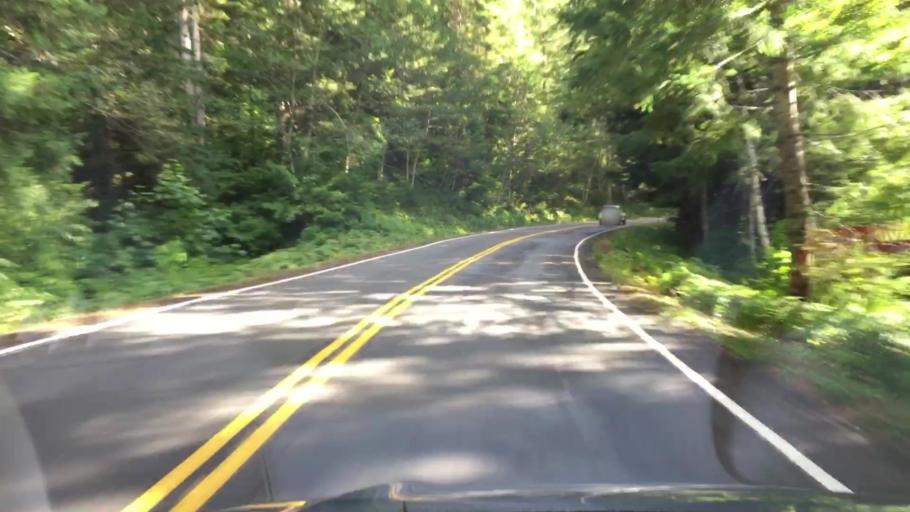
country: US
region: Washington
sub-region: Pierce County
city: Buckley
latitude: 46.7387
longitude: -121.6121
